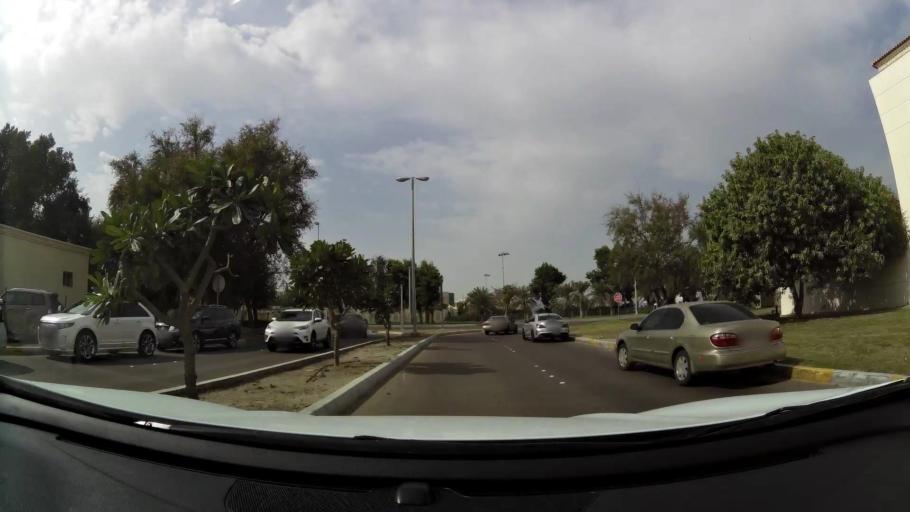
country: AE
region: Abu Dhabi
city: Abu Dhabi
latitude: 24.4461
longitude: 54.3856
